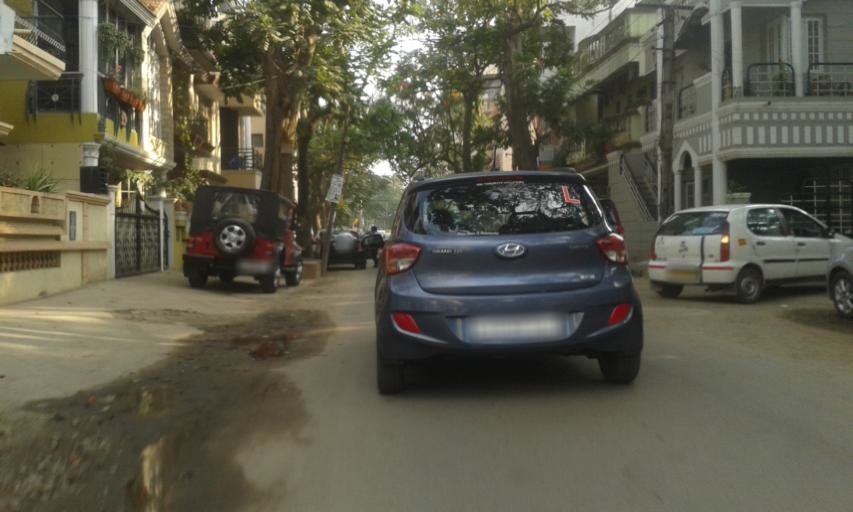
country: IN
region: Karnataka
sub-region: Bangalore Urban
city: Bangalore
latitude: 12.9697
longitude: 77.6326
